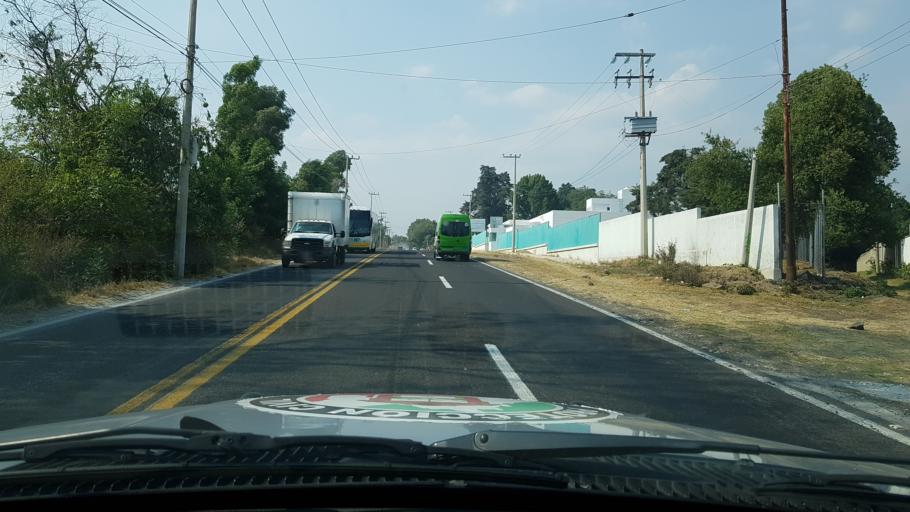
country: MX
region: Mexico
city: Tepetlixpa
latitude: 19.0158
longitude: -98.8244
